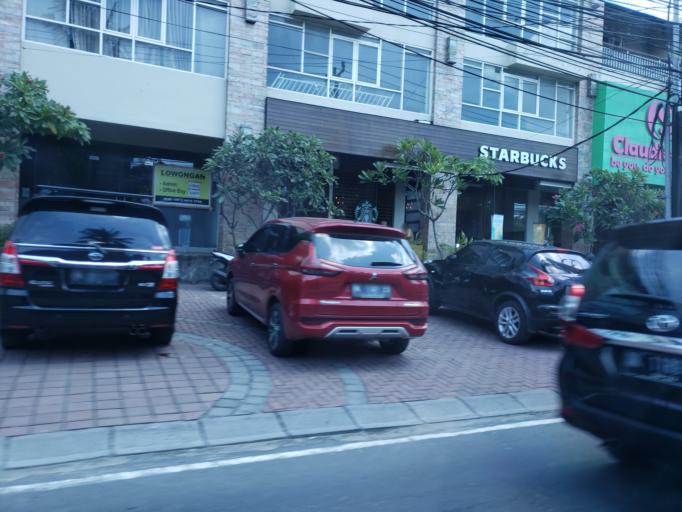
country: ID
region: Bali
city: Jimbaran
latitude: -8.7823
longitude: 115.1672
